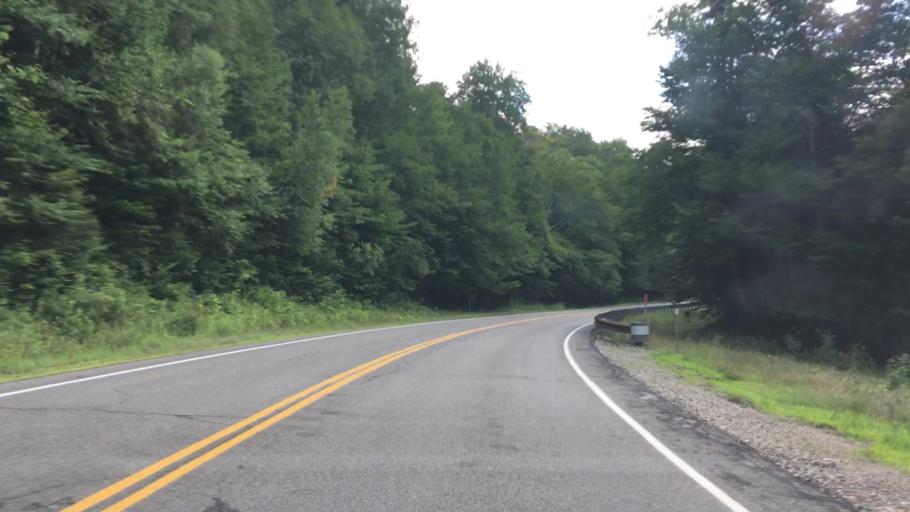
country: US
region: New Hampshire
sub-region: Grafton County
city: Woodstock
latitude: 44.0595
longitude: -71.7924
